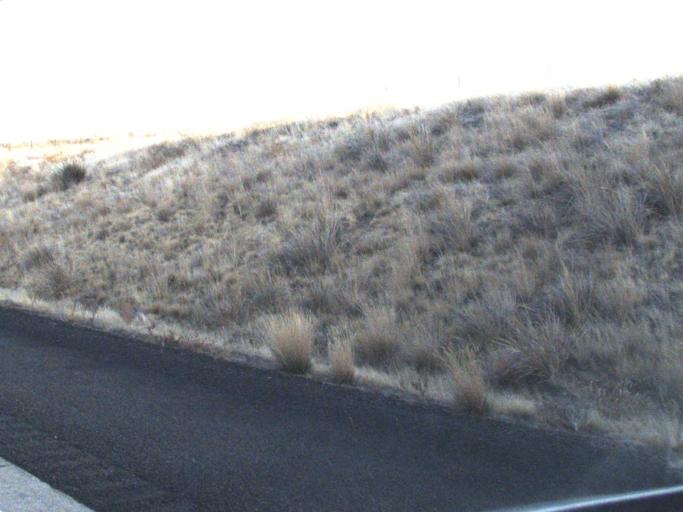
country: US
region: Washington
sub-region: Adams County
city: Ritzville
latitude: 46.9105
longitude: -118.6077
